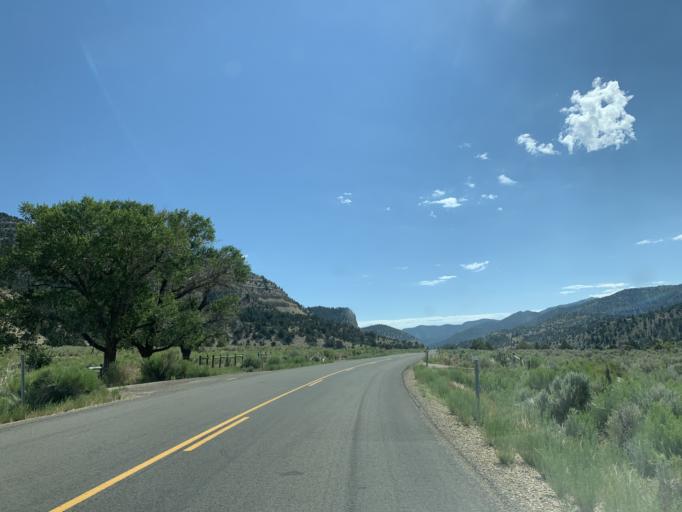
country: US
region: Utah
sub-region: Carbon County
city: East Carbon City
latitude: 39.7764
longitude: -110.5003
